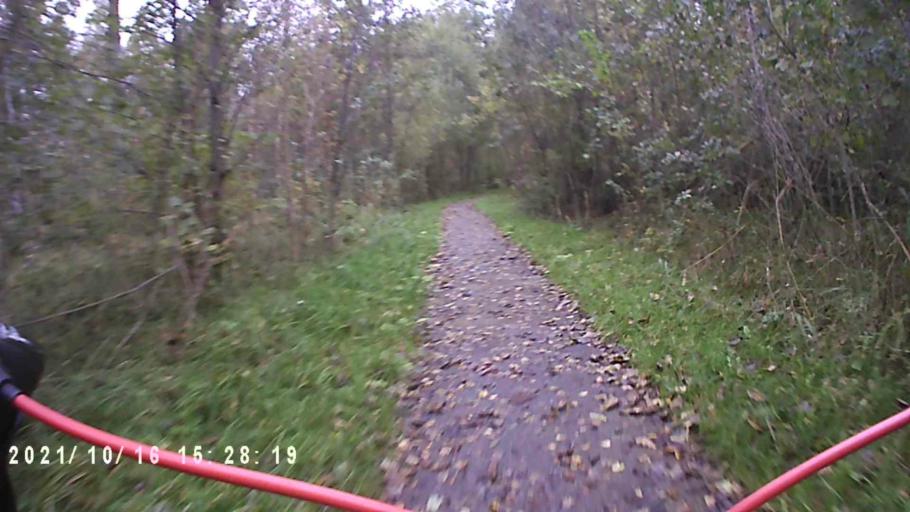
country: NL
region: Friesland
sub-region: Gemeente Dongeradeel
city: Anjum
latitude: 53.4048
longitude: 6.2260
